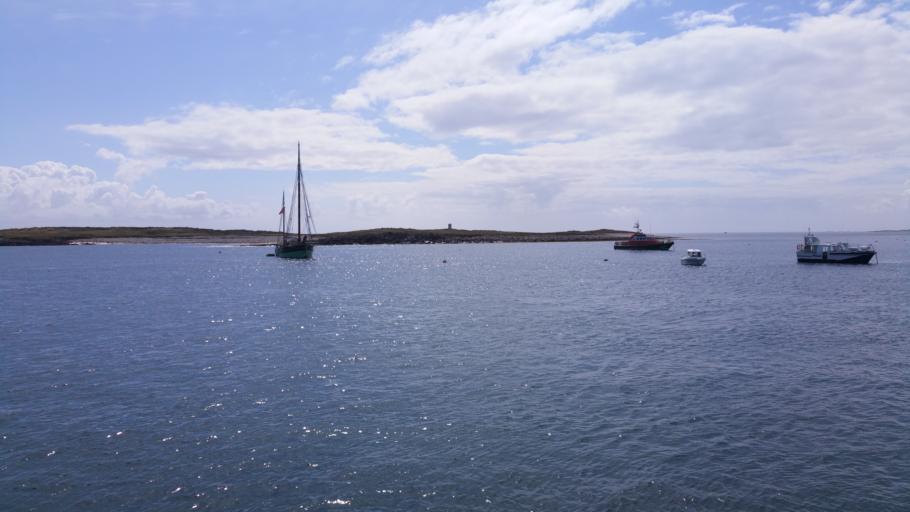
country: FR
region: Brittany
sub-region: Departement du Finistere
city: Le Conquet
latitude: 48.4021
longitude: -4.9568
